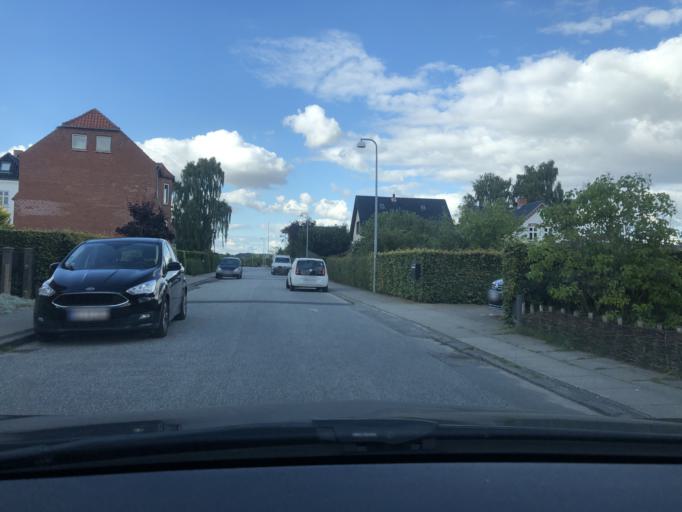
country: DK
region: South Denmark
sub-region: Vejle Kommune
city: Vejle
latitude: 55.6977
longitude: 9.5293
